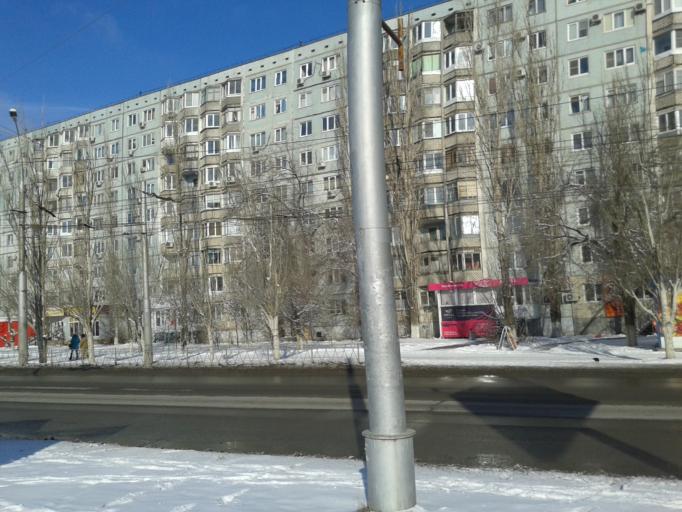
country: RU
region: Volgograd
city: Volgograd
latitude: 48.7504
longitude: 44.4974
